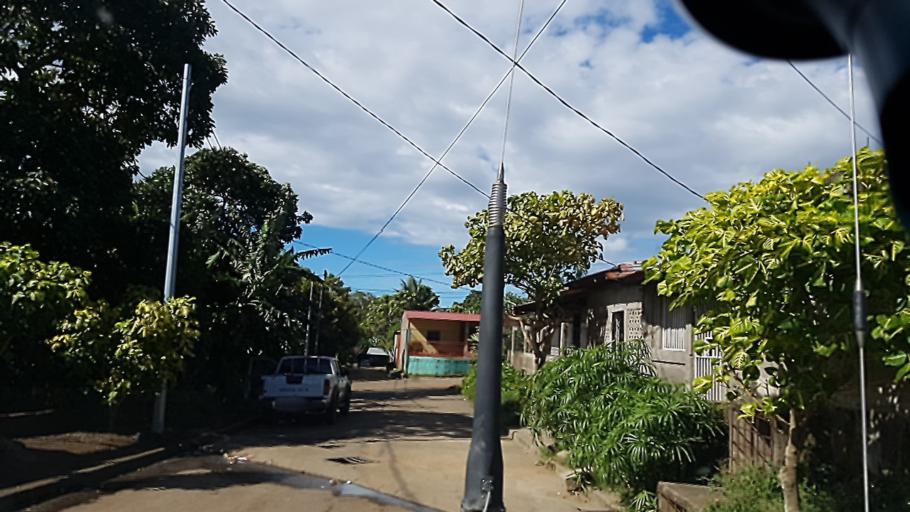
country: NI
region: Carazo
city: Dolores
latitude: 11.8575
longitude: -86.2175
